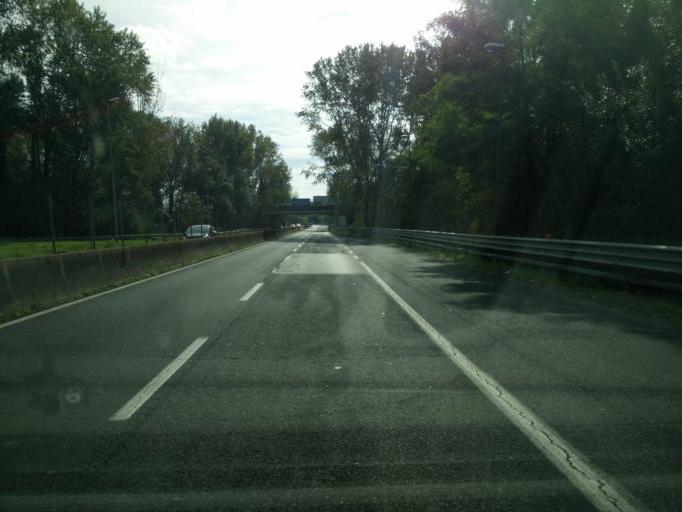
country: IT
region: Tuscany
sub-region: Provincia di Siena
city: Siena
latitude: 43.3098
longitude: 11.3127
